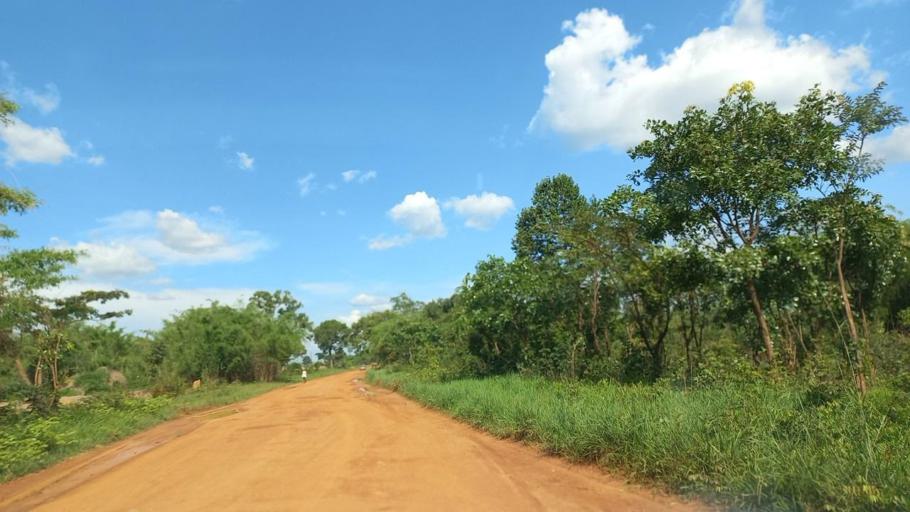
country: ZM
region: Copperbelt
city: Kitwe
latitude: -12.8640
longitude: 28.3769
